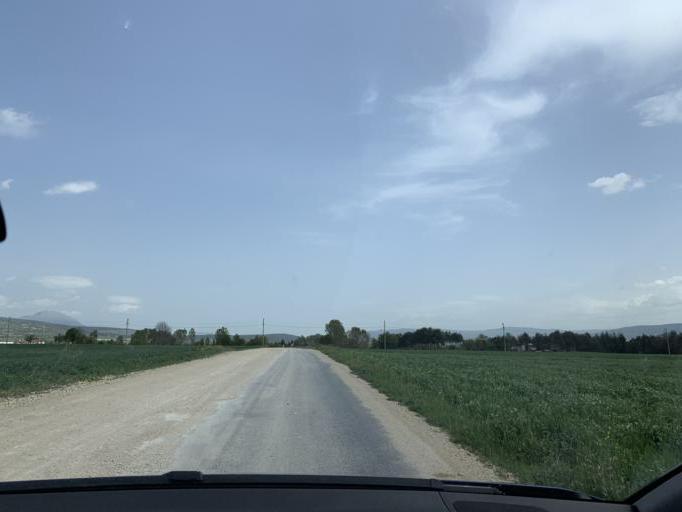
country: TR
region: Bolu
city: Bolu
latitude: 40.7515
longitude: 31.6714
